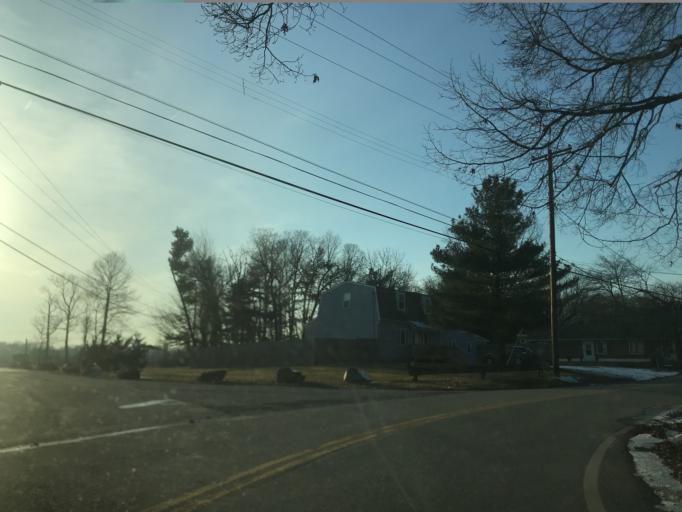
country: US
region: Maryland
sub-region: Harford County
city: Edgewood
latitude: 39.4020
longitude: -76.3263
